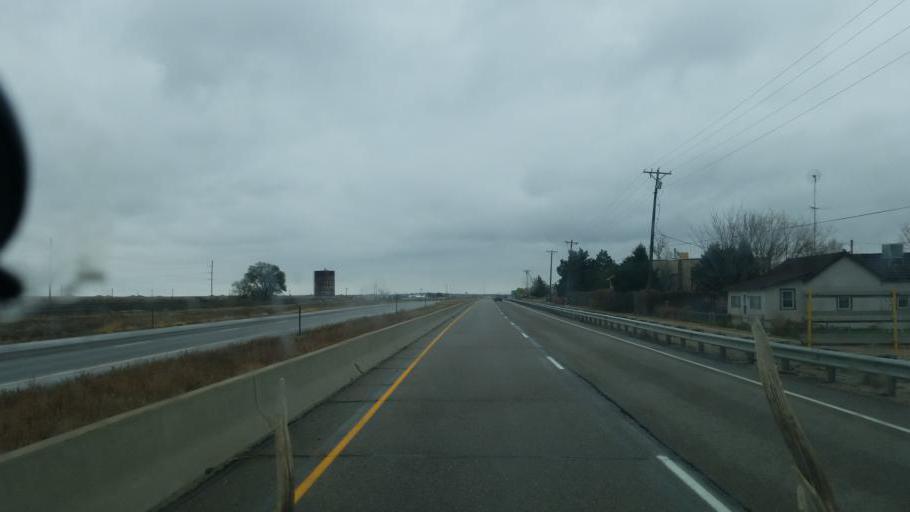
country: US
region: Colorado
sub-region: Pueblo County
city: Pueblo
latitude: 38.2752
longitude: -104.4638
